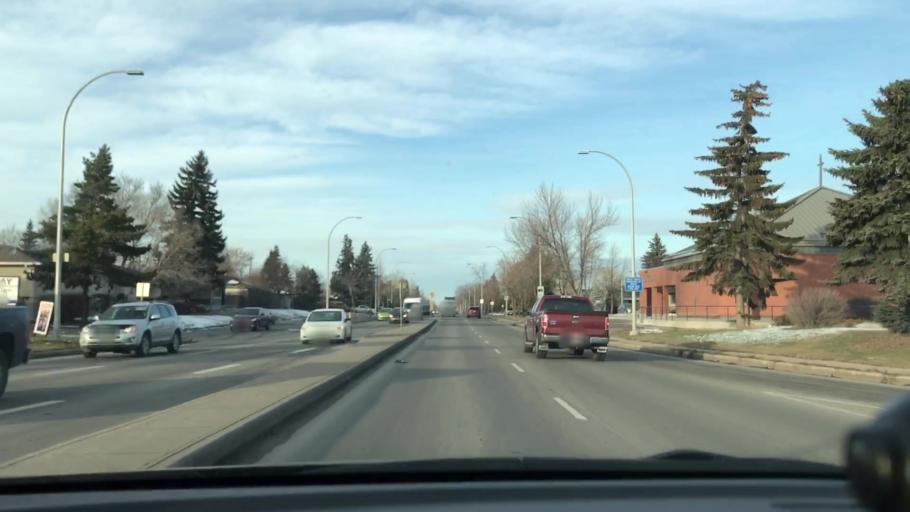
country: CA
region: Alberta
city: Edmonton
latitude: 53.5257
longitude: -113.4428
